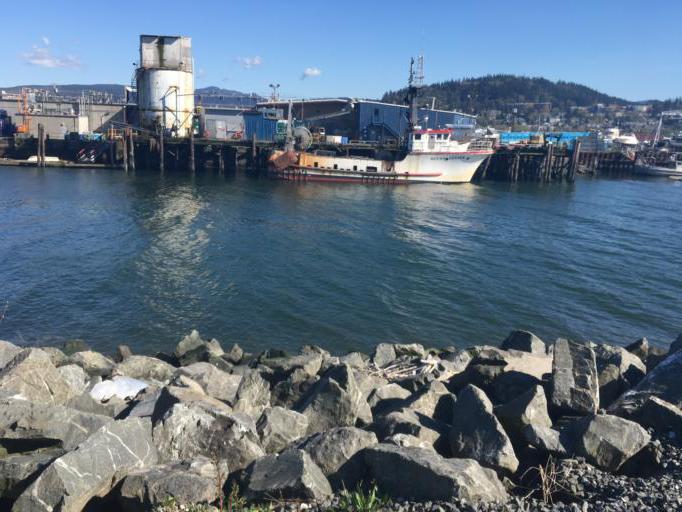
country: US
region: Washington
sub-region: Whatcom County
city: Bellingham
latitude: 48.7549
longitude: -122.4942
